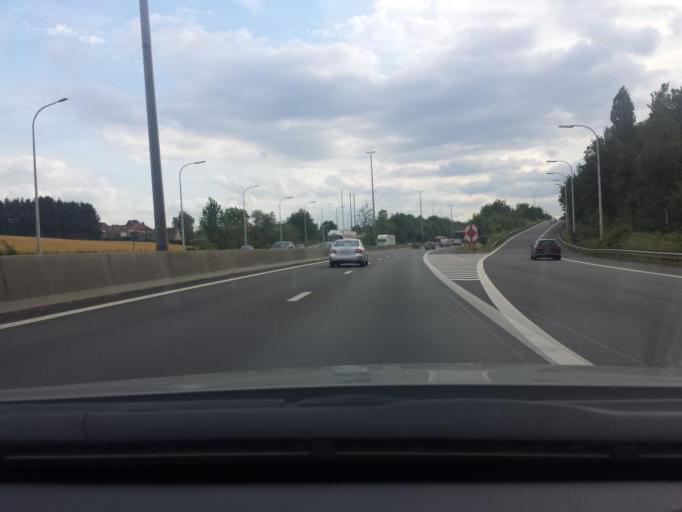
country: BE
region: Flanders
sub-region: Provincie Vlaams-Brabant
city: Leuven
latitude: 50.8964
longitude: 4.6929
